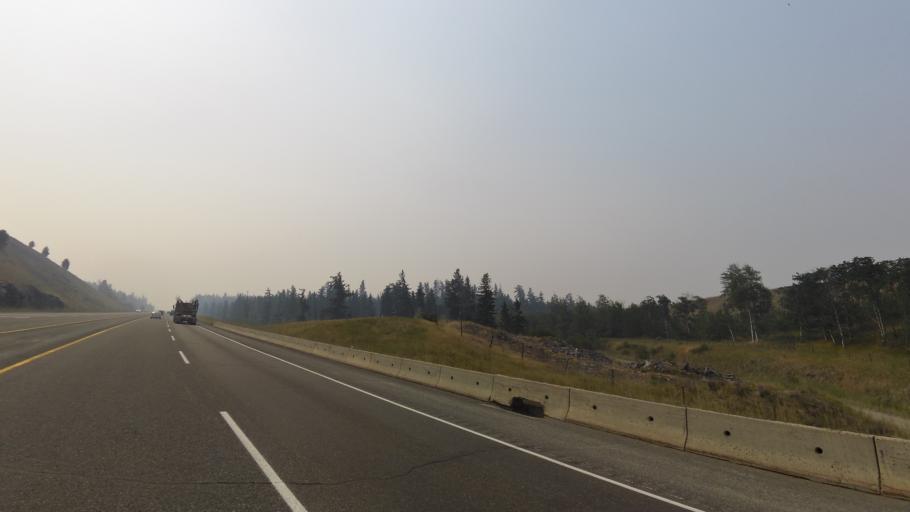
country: CA
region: British Columbia
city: Merritt
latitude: 50.0966
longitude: -120.6769
